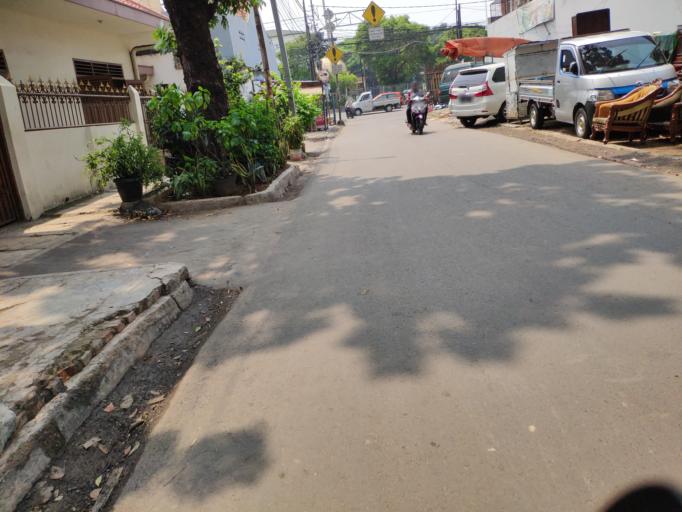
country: ID
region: Jakarta Raya
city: Jakarta
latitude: -6.2056
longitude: 106.8588
